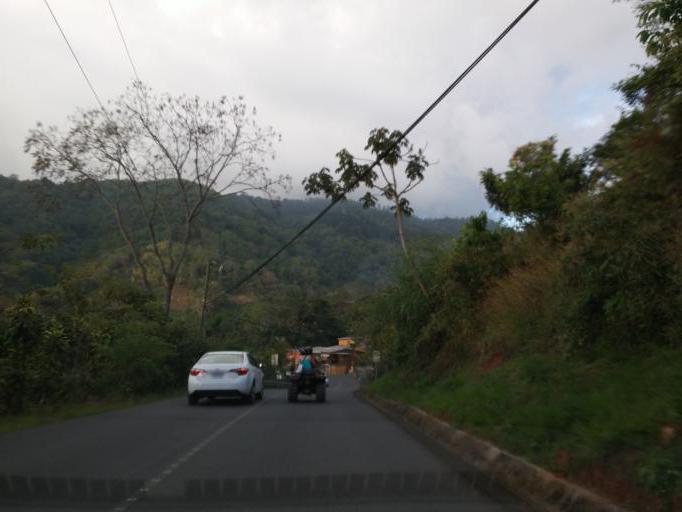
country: CR
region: San Jose
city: Palmichal
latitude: 9.8369
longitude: -84.2057
